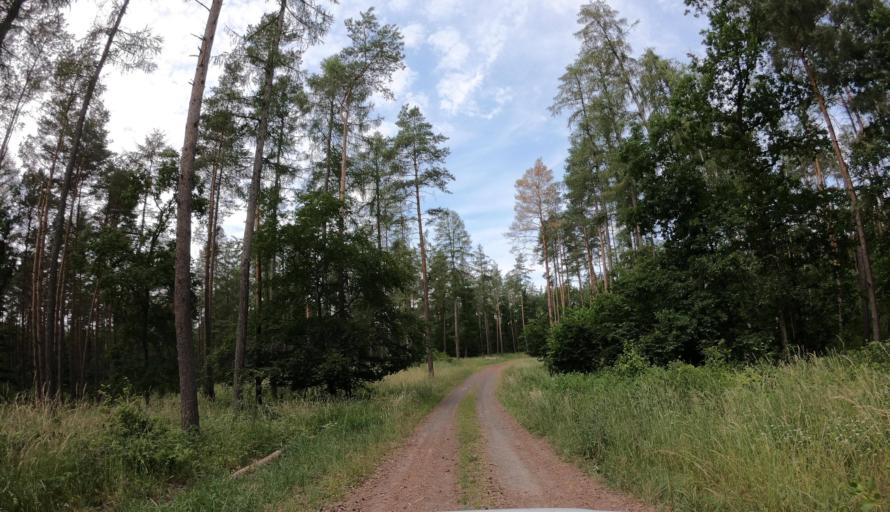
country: PL
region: West Pomeranian Voivodeship
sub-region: Powiat gryfinski
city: Banie
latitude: 53.0266
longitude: 14.7429
